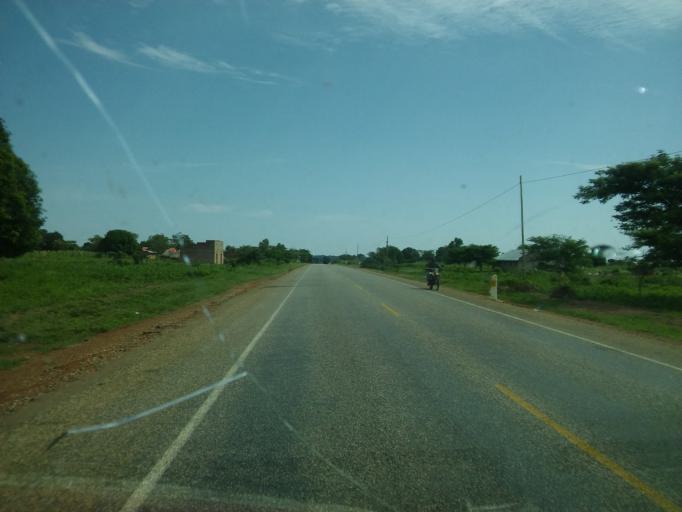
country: UG
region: Eastern Region
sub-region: Bukedea District
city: Bukedea
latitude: 1.3158
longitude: 34.0621
